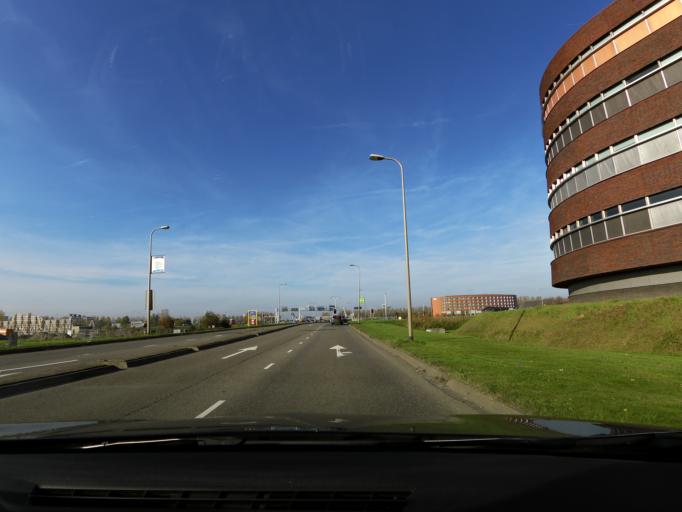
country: NL
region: South Holland
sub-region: Gemeente Barendrecht
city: Barendrecht
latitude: 51.8641
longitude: 4.5570
